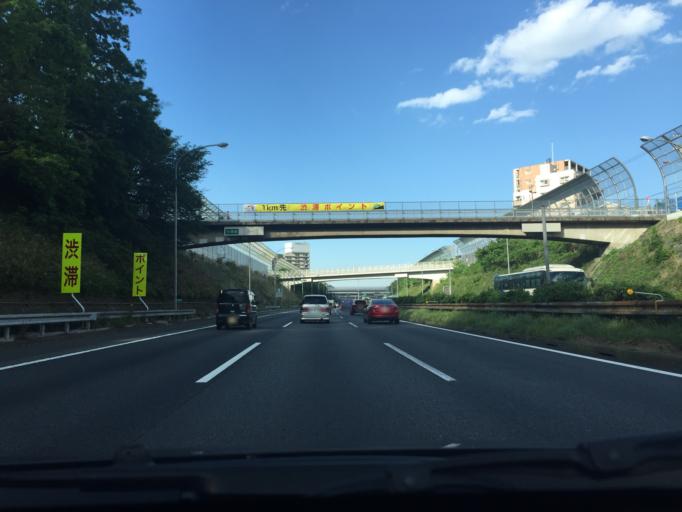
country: JP
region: Kanagawa
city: Minami-rinkan
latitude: 35.4664
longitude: 139.4373
